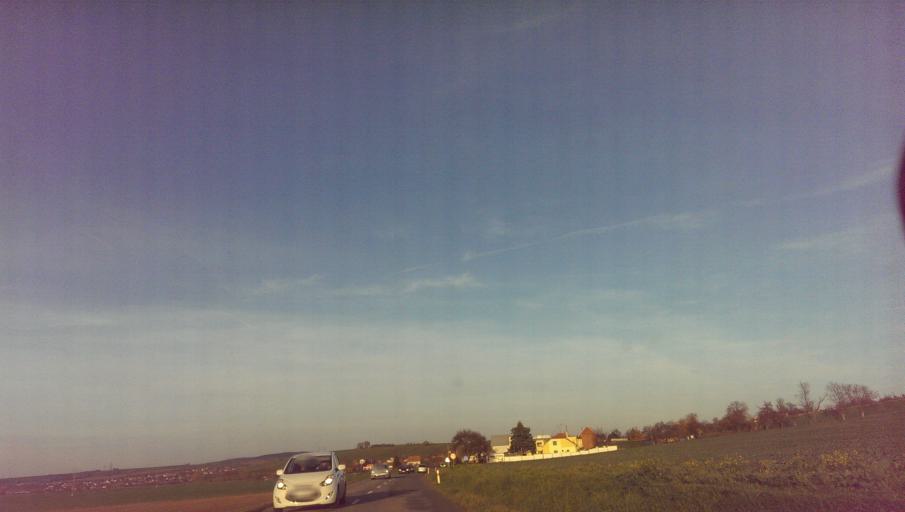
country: CZ
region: Zlin
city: Mistrice
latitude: 49.0942
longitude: 17.5279
